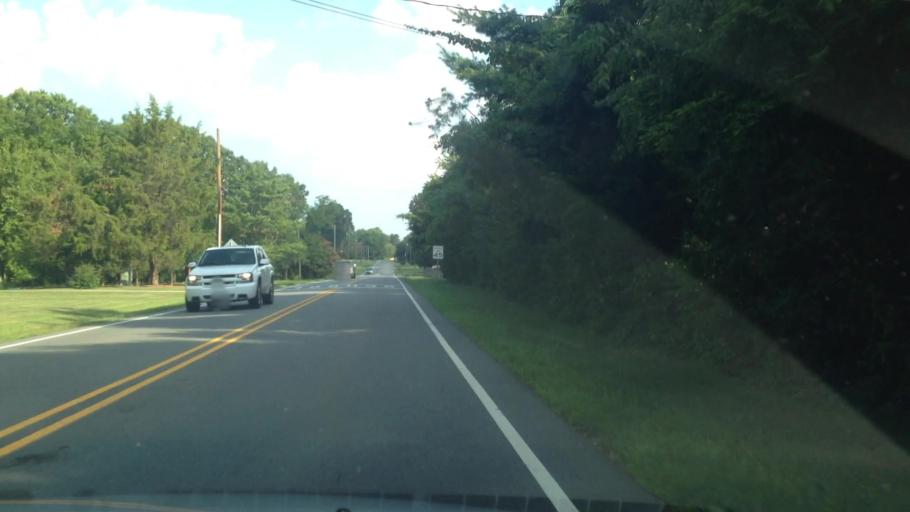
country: US
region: North Carolina
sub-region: Forsyth County
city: Walkertown
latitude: 36.1394
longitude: -80.1230
